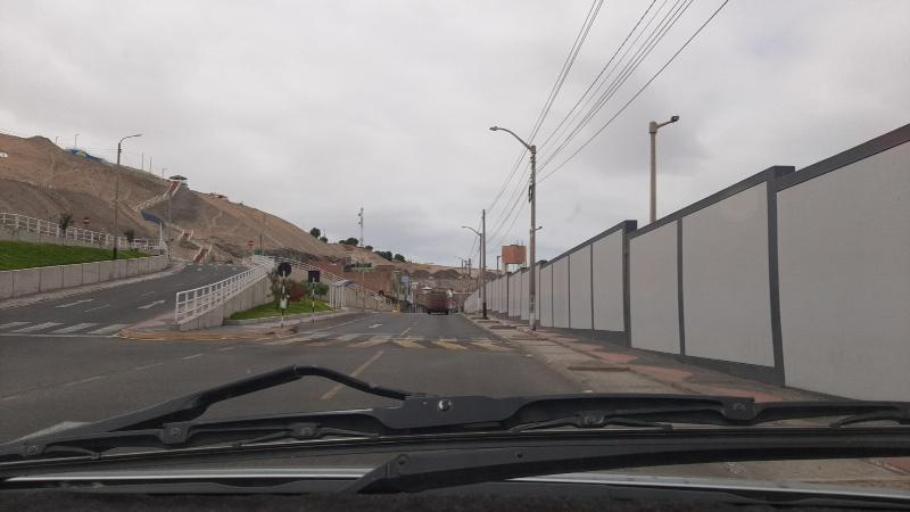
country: PE
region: Moquegua
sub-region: Provincia de Ilo
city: Ilo
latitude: -17.6510
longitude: -71.3407
